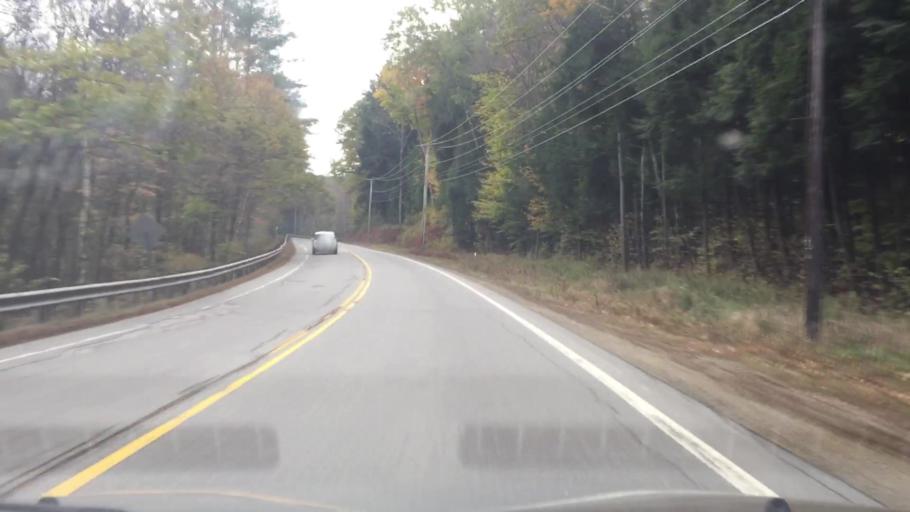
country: US
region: New Hampshire
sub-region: Cheshire County
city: Keene
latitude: 43.0351
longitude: -72.2697
